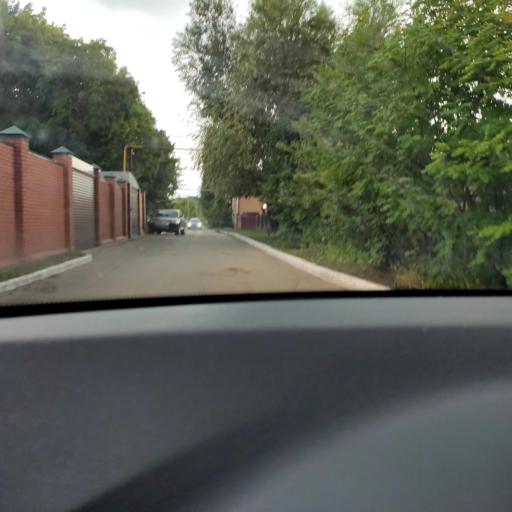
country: RU
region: Samara
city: Samara
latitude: 53.2632
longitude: 50.2035
